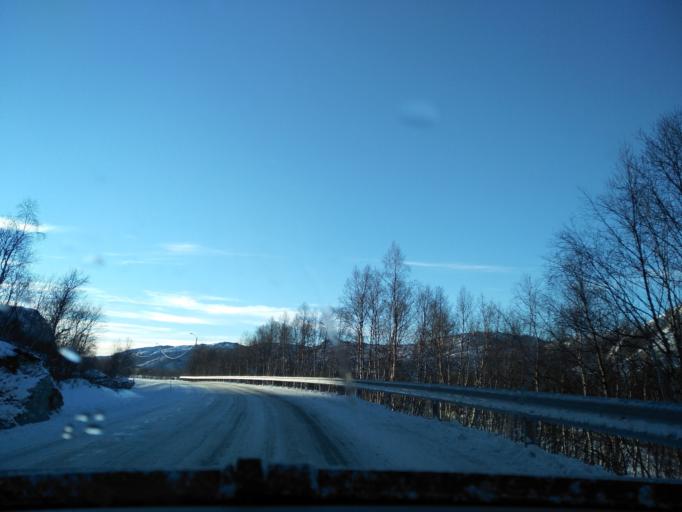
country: NO
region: Vest-Agder
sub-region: Sirdal
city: Tonstad
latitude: 59.0092
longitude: 6.9332
